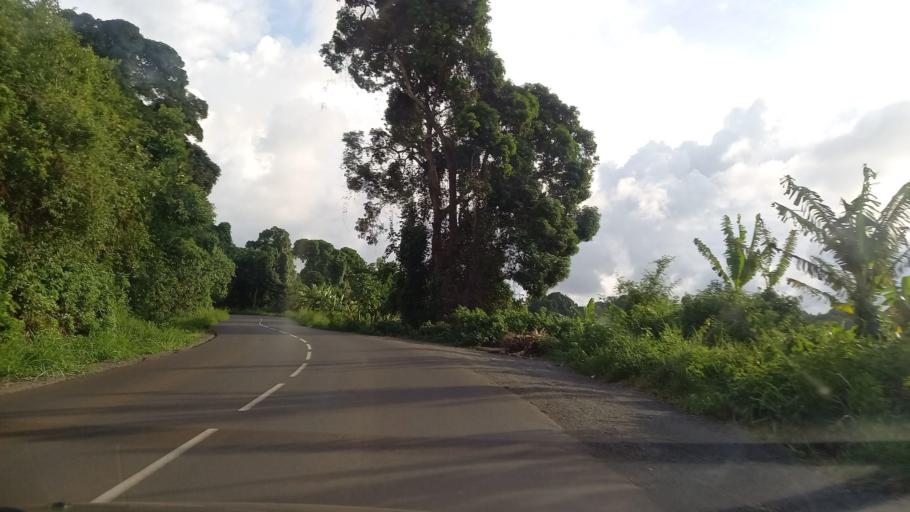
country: YT
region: Bandraboua
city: Bandraboua
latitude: -12.7377
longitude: 45.1178
